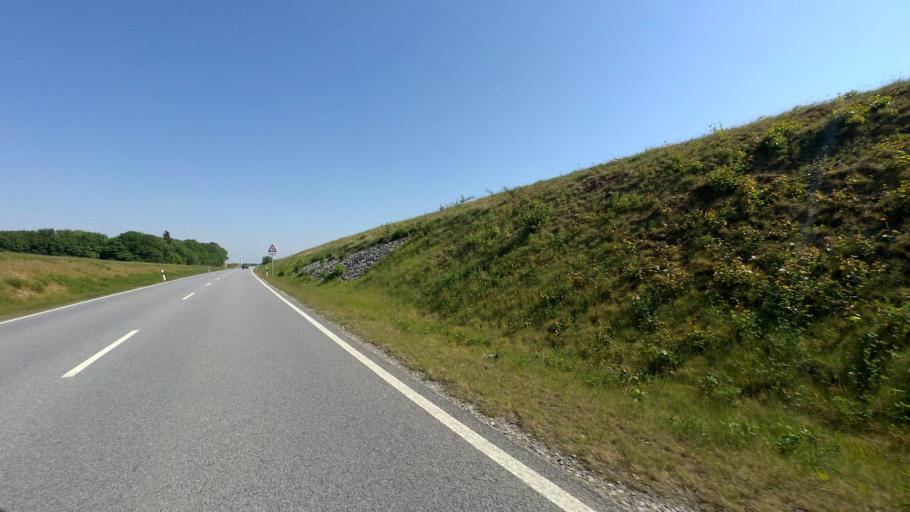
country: DE
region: Saxony
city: Elstra
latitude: 51.2047
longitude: 14.1507
